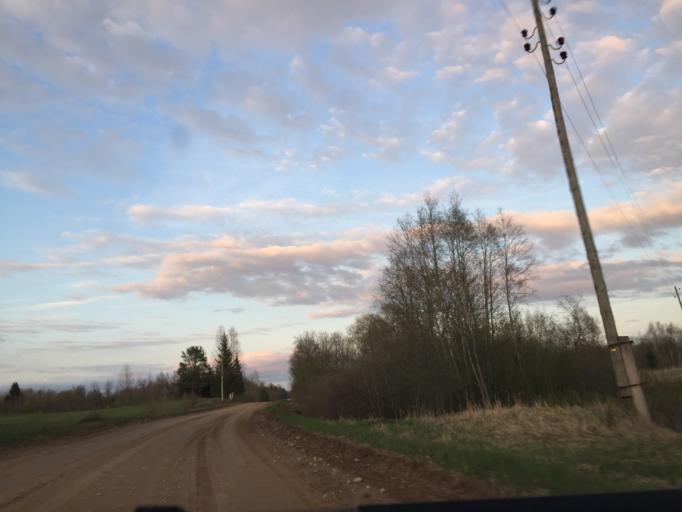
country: LV
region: Gulbenes Rajons
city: Gulbene
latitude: 57.2433
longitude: 26.8235
